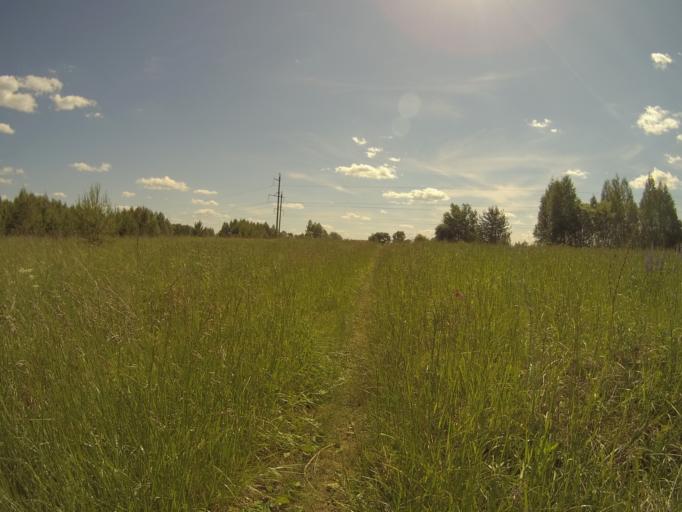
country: RU
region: Vladimir
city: Golovino
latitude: 55.9875
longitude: 40.4036
